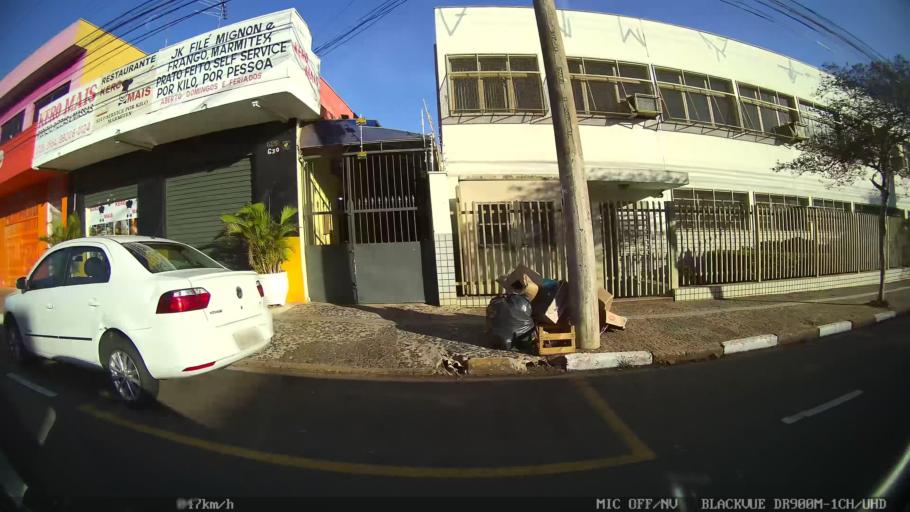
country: BR
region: Sao Paulo
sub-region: Franca
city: Franca
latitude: -20.5270
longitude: -47.3861
